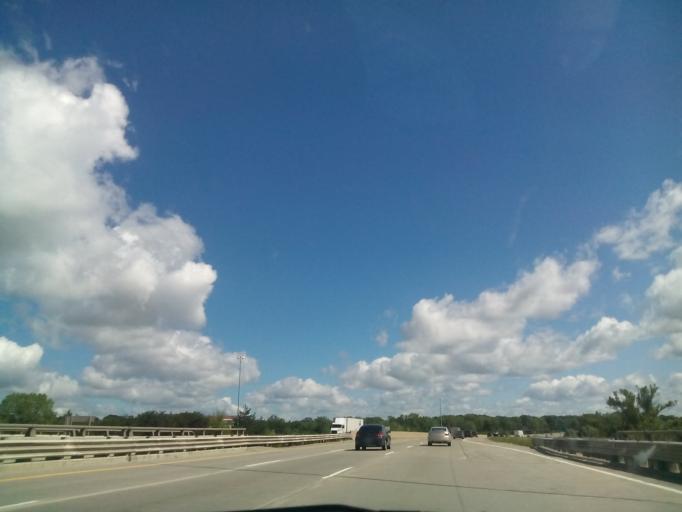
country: US
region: Michigan
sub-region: Genesee County
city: Flint
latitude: 42.9968
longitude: -83.7059
